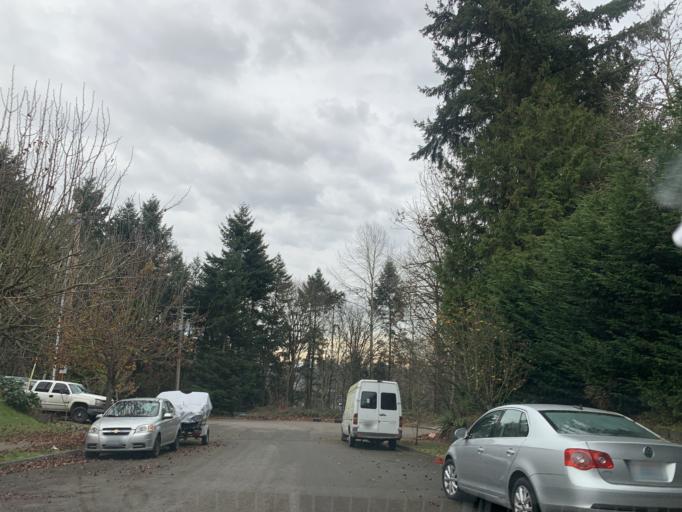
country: US
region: Washington
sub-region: King County
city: Lakeland North
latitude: 47.3349
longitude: -122.2952
